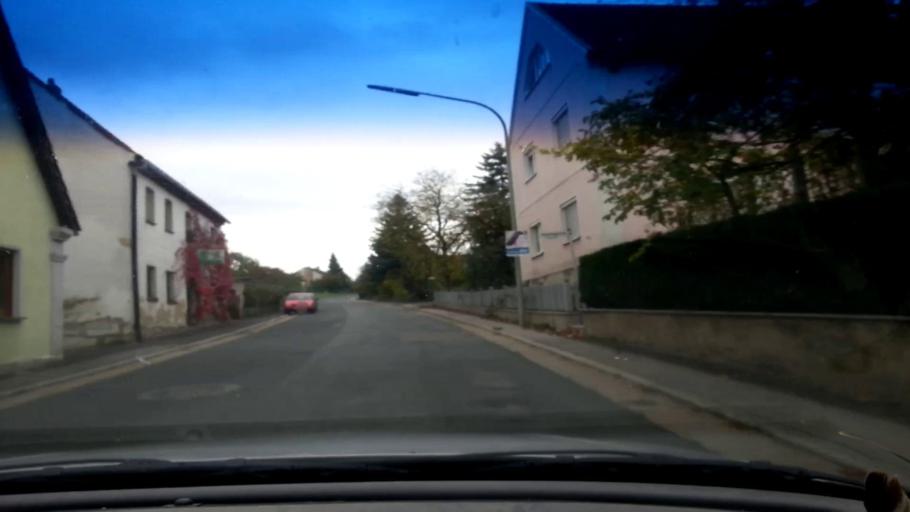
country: DE
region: Bavaria
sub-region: Upper Franconia
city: Priesendorf
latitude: 49.9058
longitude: 10.6710
